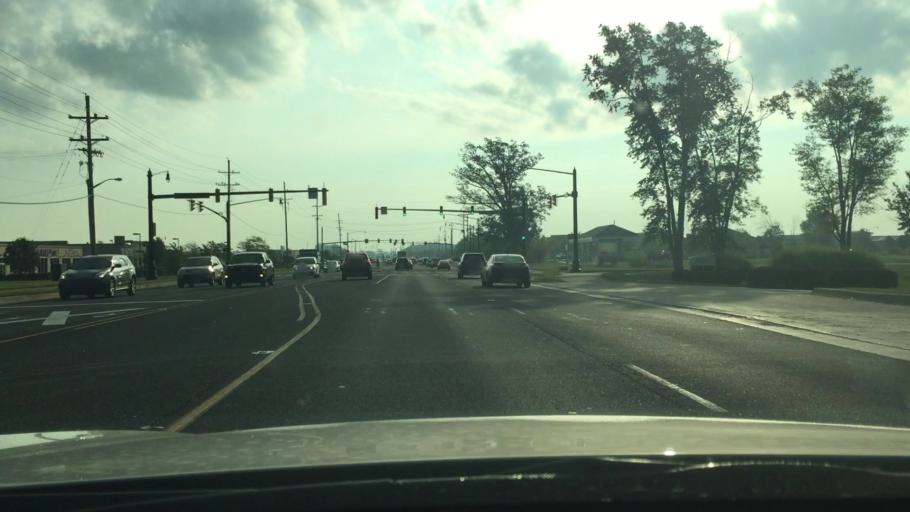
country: US
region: Indiana
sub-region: Hamilton County
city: Noblesville
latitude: 40.0008
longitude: -86.0077
